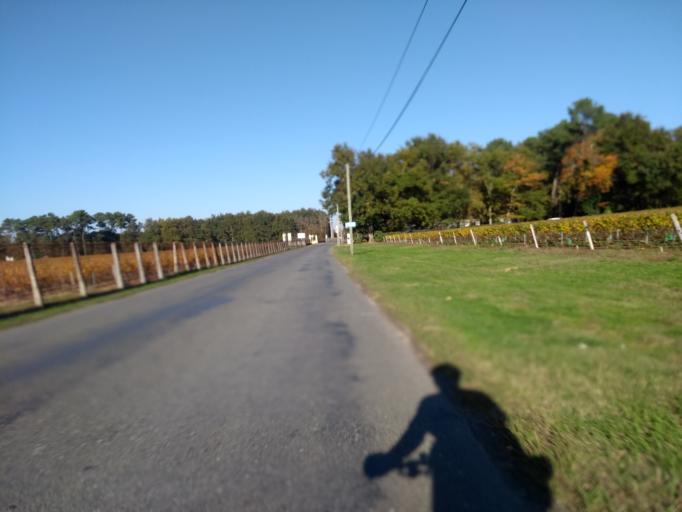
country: FR
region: Aquitaine
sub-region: Departement de la Gironde
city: Ayguemorte-les-Graves
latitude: 44.6981
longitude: -0.4820
